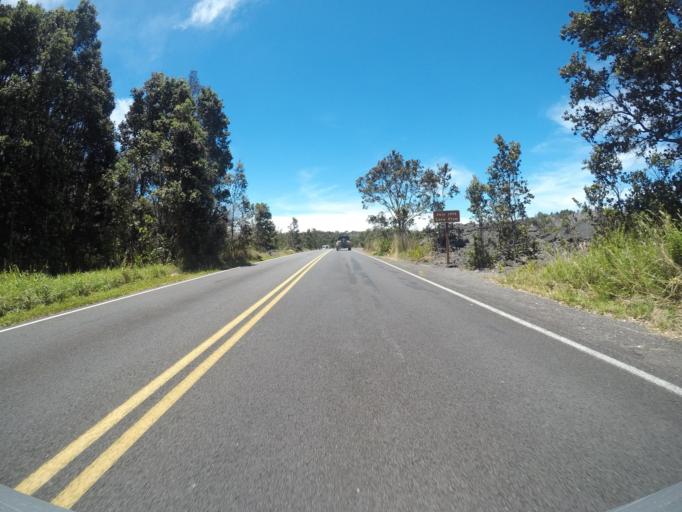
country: US
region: Hawaii
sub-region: Hawaii County
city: Volcano
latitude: 19.4005
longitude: -155.2534
